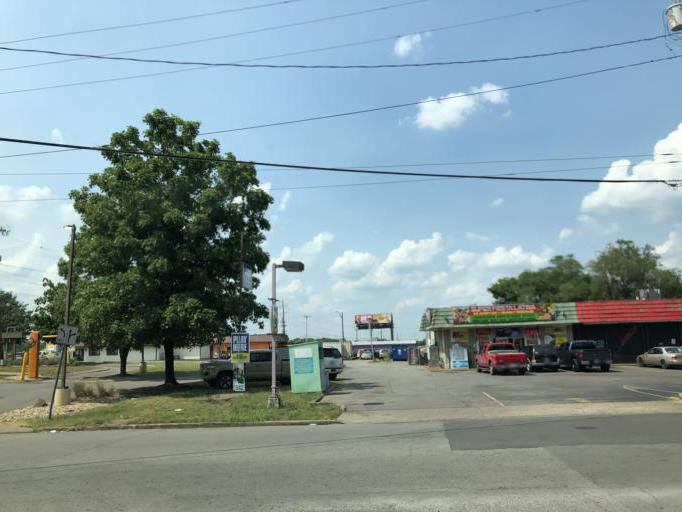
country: US
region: Tennessee
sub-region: Davidson County
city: Goodlettsville
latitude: 36.2479
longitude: -86.7191
